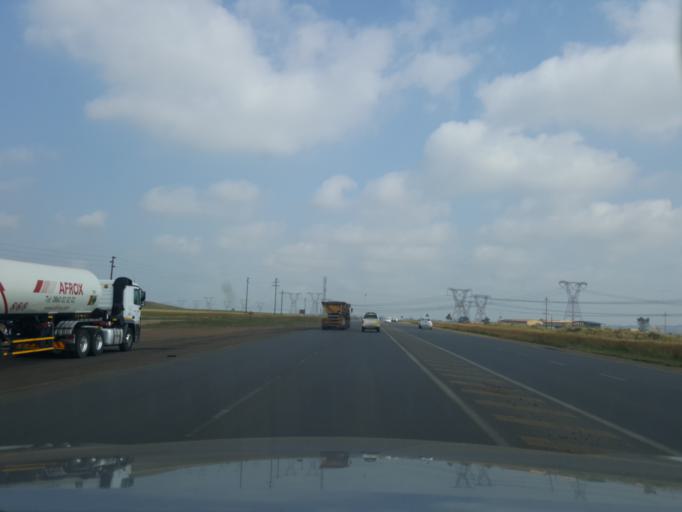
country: ZA
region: Mpumalanga
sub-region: Nkangala District Municipality
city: Witbank
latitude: -25.9757
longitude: 29.2768
